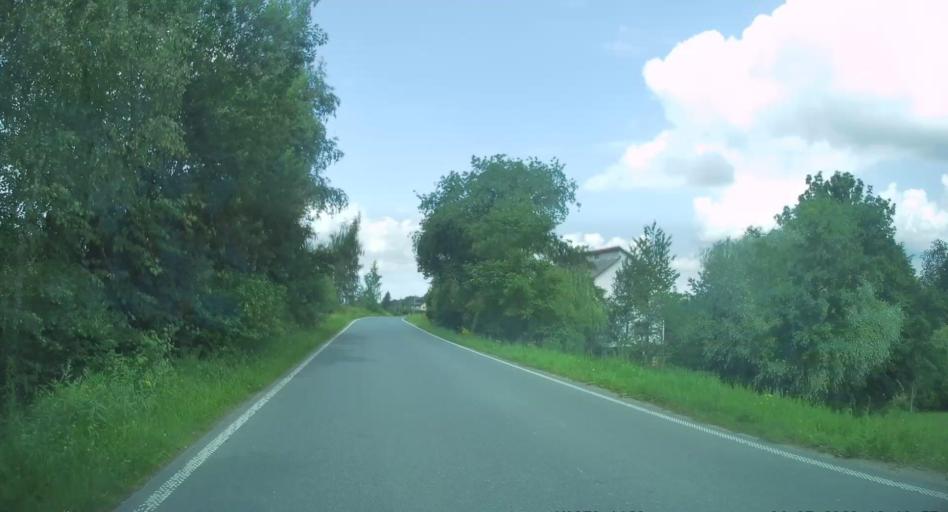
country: PL
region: Lesser Poland Voivodeship
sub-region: Powiat nowosadecki
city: Korzenna
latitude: 49.6922
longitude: 20.7741
